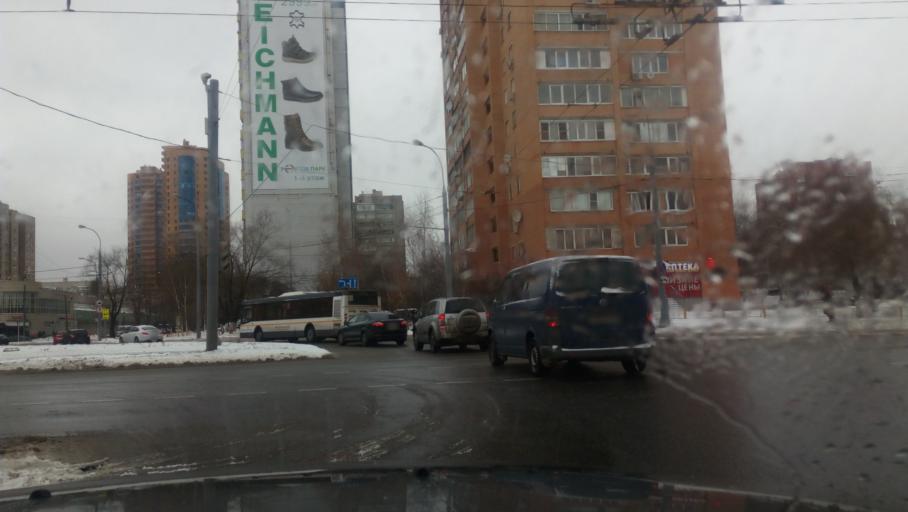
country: RU
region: Moskovskaya
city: Reutov
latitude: 55.7453
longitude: 37.8646
